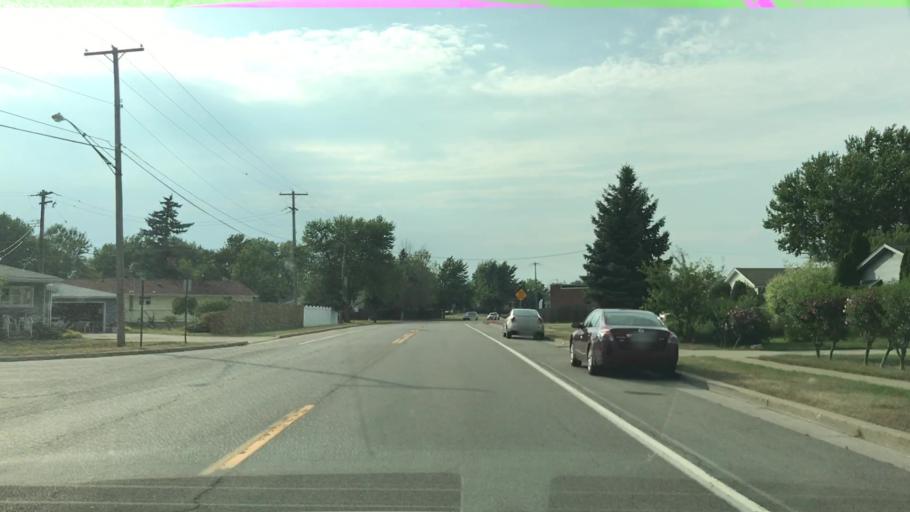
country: US
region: New York
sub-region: Erie County
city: Depew
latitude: 42.9174
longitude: -78.7122
